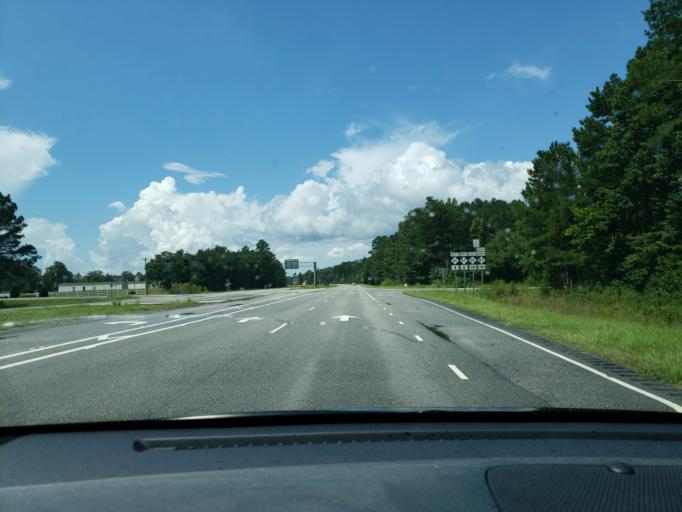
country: US
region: North Carolina
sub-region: Bladen County
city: Elizabethtown
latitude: 34.6416
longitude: -78.6747
